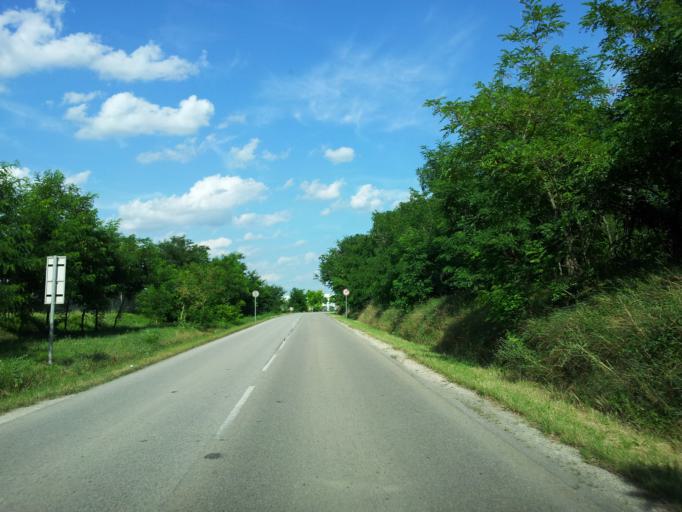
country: HU
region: Pest
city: Dunavarsany
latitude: 47.2627
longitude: 19.0224
